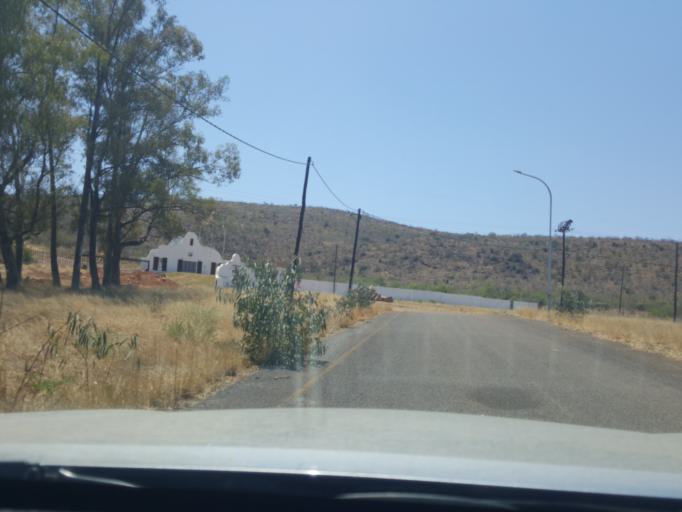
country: BW
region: South East
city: Lobatse
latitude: -25.1915
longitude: 25.6734
